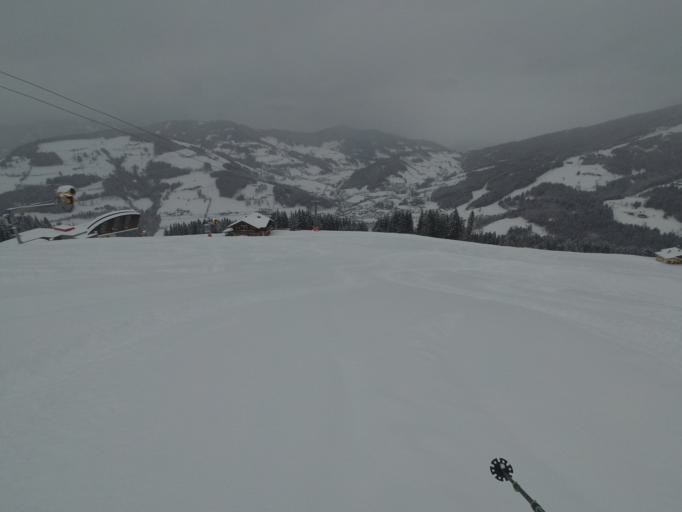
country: AT
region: Salzburg
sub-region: Politischer Bezirk Sankt Johann im Pongau
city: Wagrain
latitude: 47.3214
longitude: 13.2914
